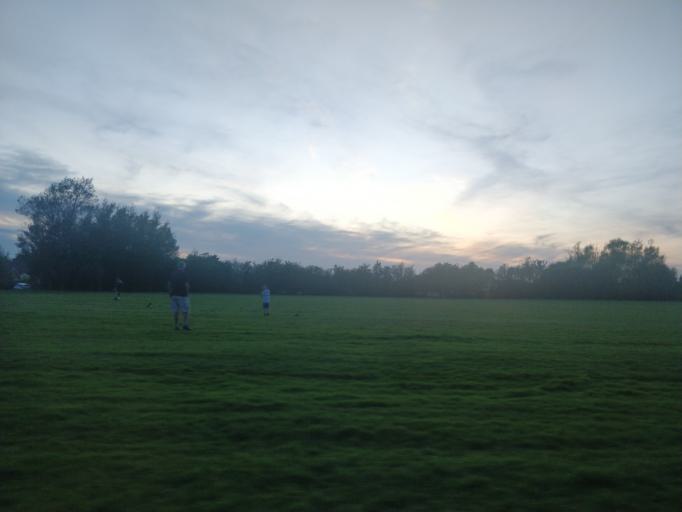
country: GB
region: England
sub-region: Lancashire
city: Tarleton
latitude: 53.6989
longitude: -2.8028
